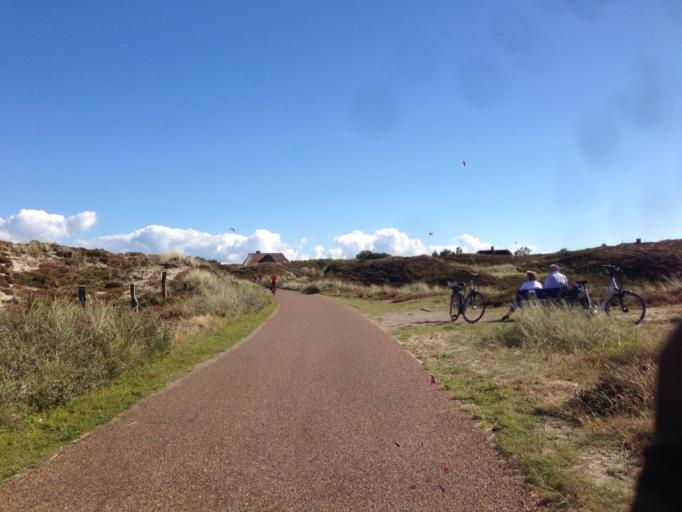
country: DE
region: Schleswig-Holstein
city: List
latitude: 55.0004
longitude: 8.3736
